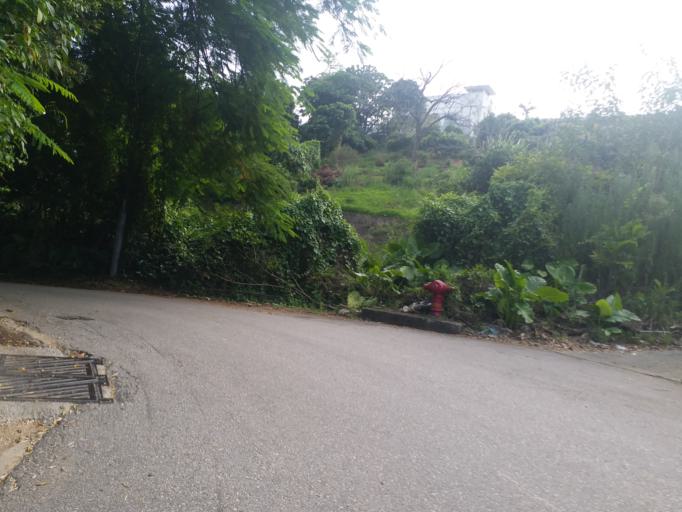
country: HK
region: Yuen Long
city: Yuen Long Kau Hui
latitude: 22.4459
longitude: 114.0111
